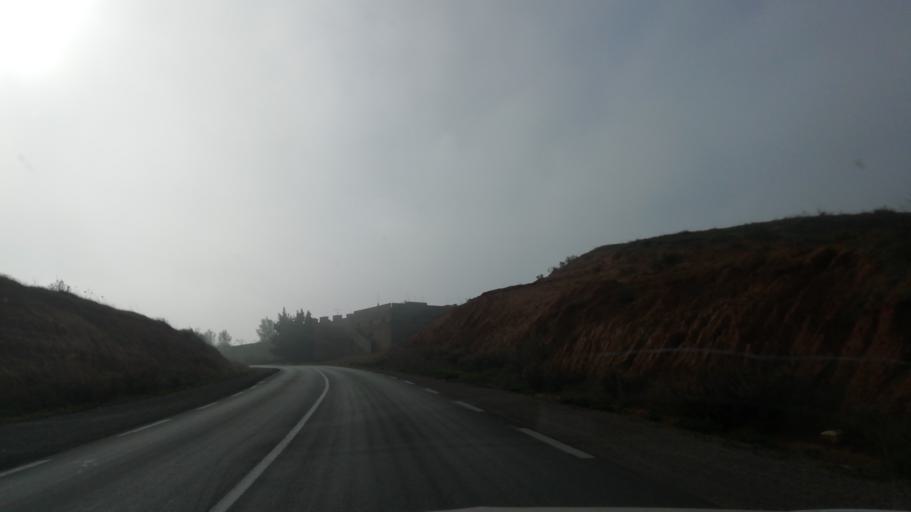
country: DZ
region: Mascara
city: Mascara
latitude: 35.5338
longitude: 0.3536
